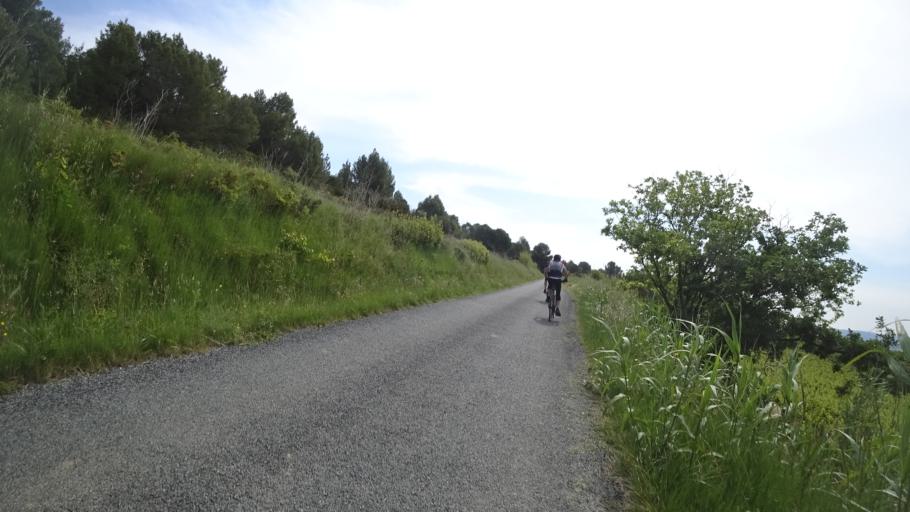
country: FR
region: Languedoc-Roussillon
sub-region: Departement de l'Aude
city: Canet
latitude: 43.2564
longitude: 2.8047
